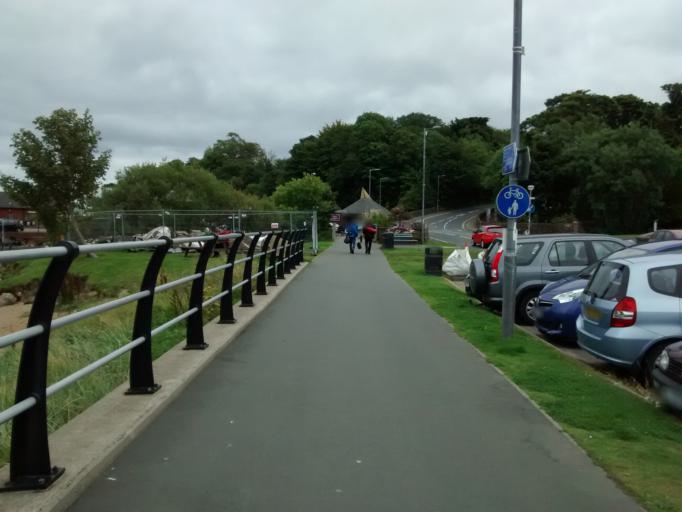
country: GB
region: Scotland
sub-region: North Ayrshire
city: Lamlash
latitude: 55.5765
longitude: -5.1410
